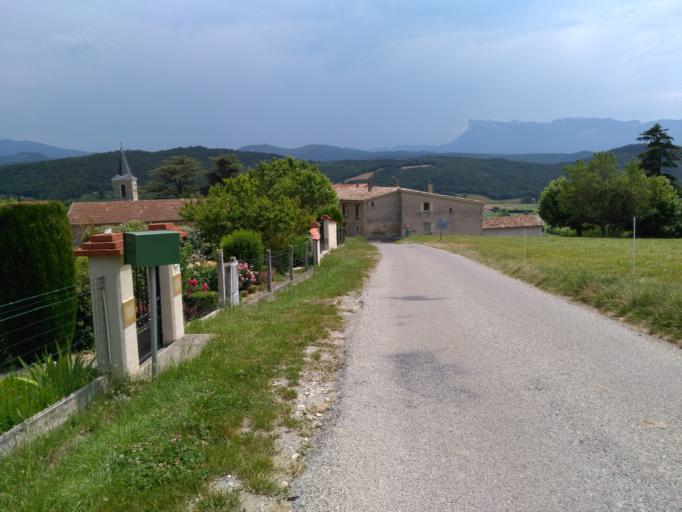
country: FR
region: Rhone-Alpes
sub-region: Departement de la Drome
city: Aouste-sur-Sye
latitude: 44.7611
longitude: 5.1105
